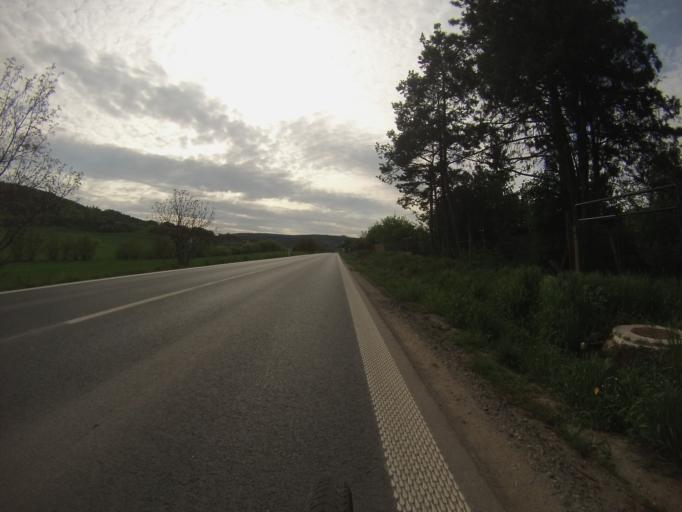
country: CZ
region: South Moravian
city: Drasov
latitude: 49.3254
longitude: 16.4505
